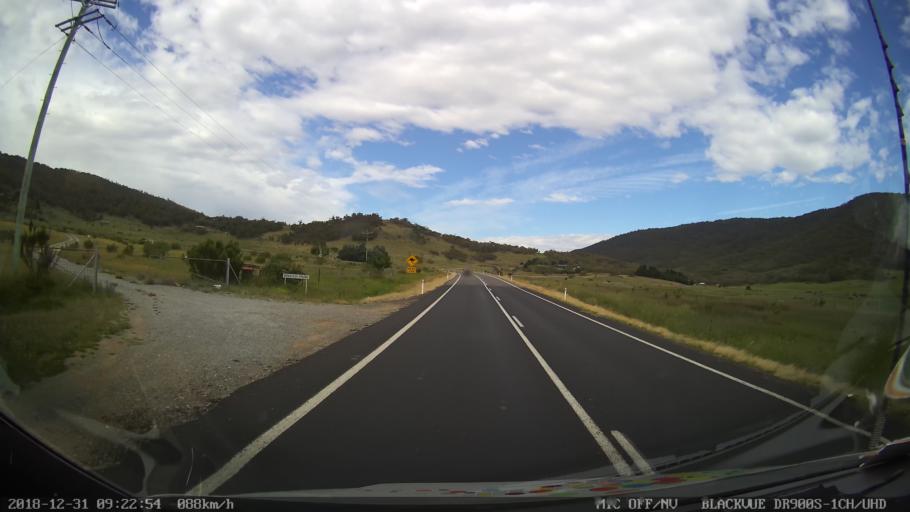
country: AU
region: New South Wales
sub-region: Snowy River
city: Jindabyne
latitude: -36.4371
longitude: 148.5410
